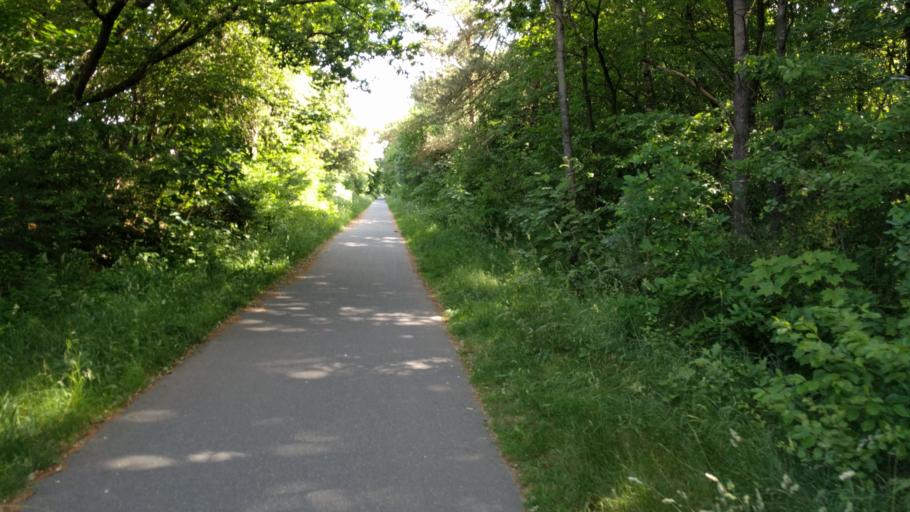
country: DK
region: Central Jutland
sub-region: Viborg Kommune
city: Viborg
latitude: 56.4257
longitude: 9.3849
